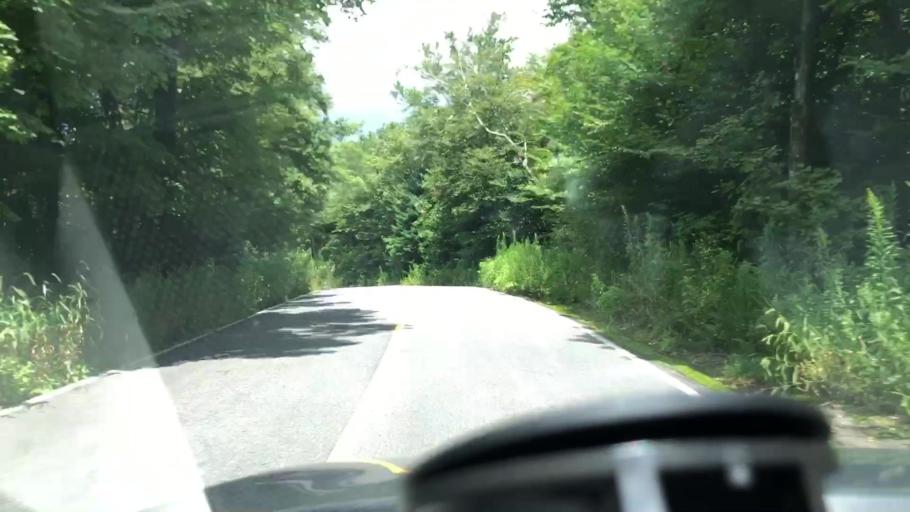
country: US
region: Massachusetts
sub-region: Berkshire County
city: Adams
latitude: 42.6493
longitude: -73.1609
